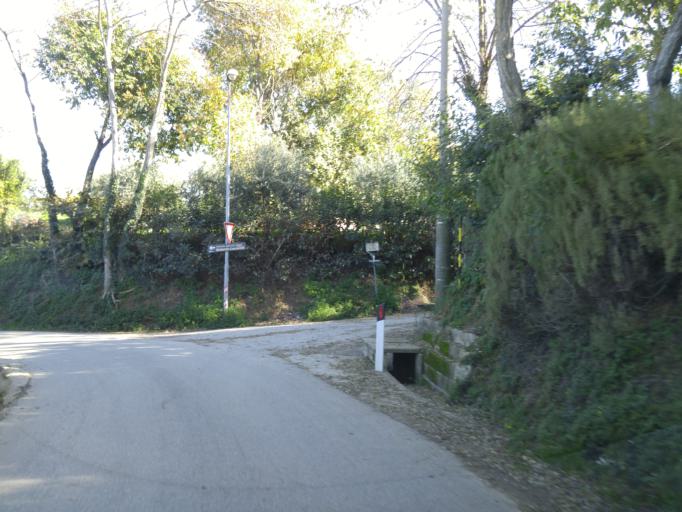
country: IT
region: The Marches
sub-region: Provincia di Pesaro e Urbino
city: Cartoceto
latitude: 43.7760
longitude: 12.8763
